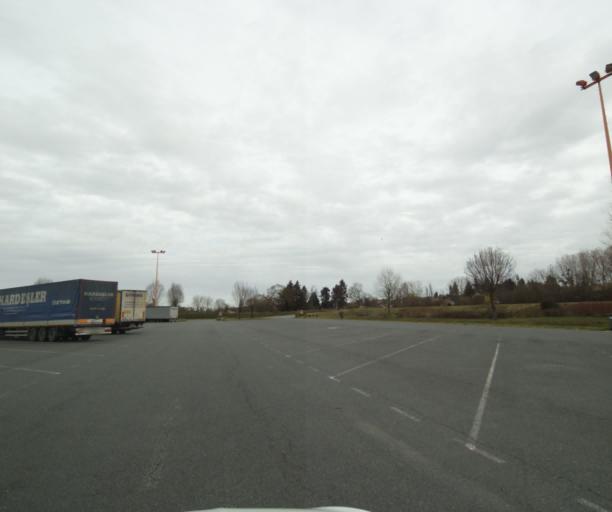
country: FR
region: Auvergne
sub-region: Departement de l'Allier
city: Toulon-sur-Allier
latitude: 46.5073
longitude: 3.3612
